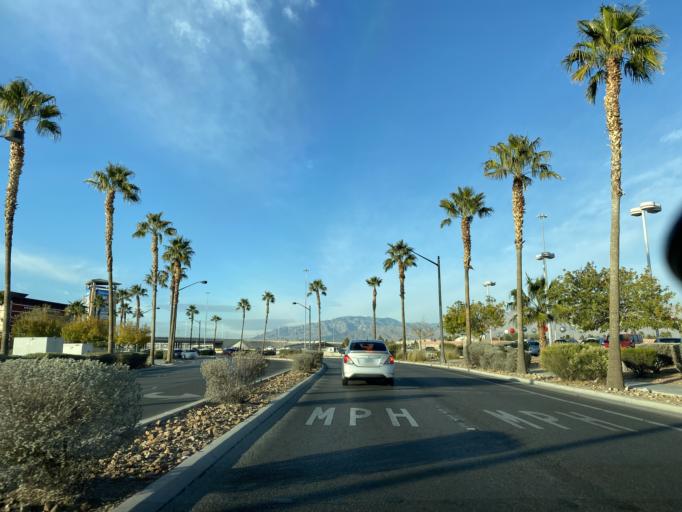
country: US
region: Nevada
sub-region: Clark County
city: Las Vegas
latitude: 36.2689
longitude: -115.2607
